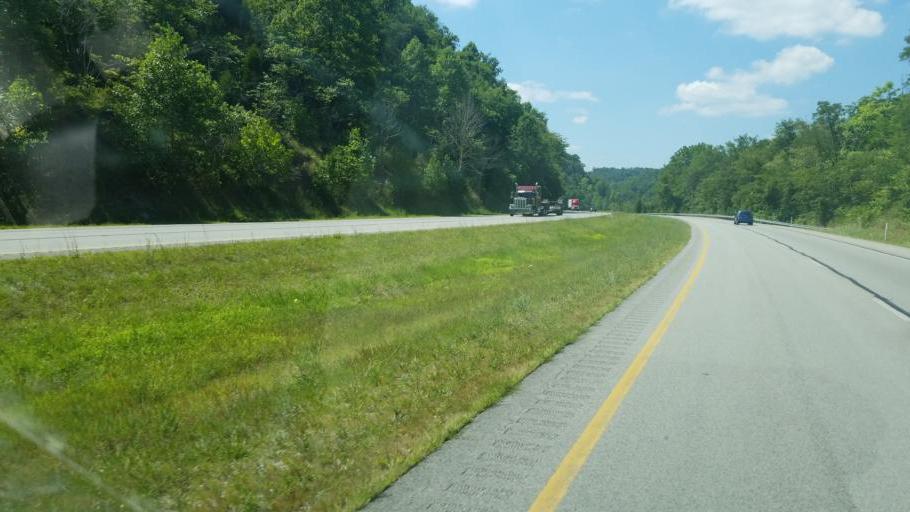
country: US
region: West Virginia
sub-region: Kanawha County
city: Sissonville
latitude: 38.5704
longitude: -81.6371
